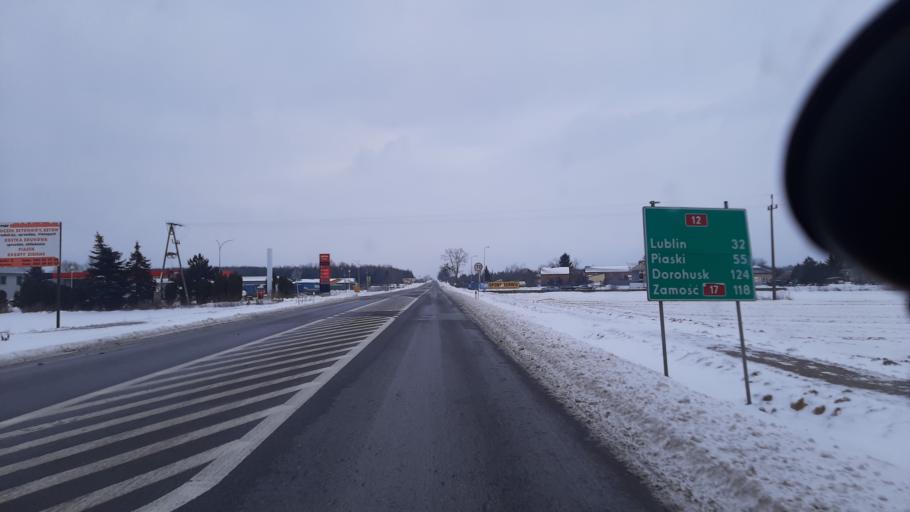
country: PL
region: Lublin Voivodeship
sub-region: Powiat pulawski
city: Kurow
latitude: 51.3866
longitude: 22.2049
